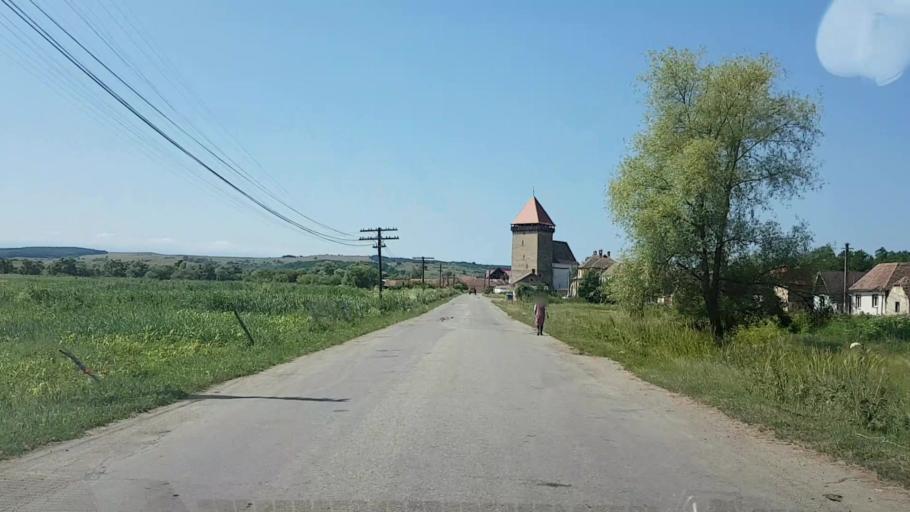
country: RO
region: Sibiu
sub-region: Comuna Bradeni
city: Bradeni
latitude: 46.0613
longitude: 24.7918
